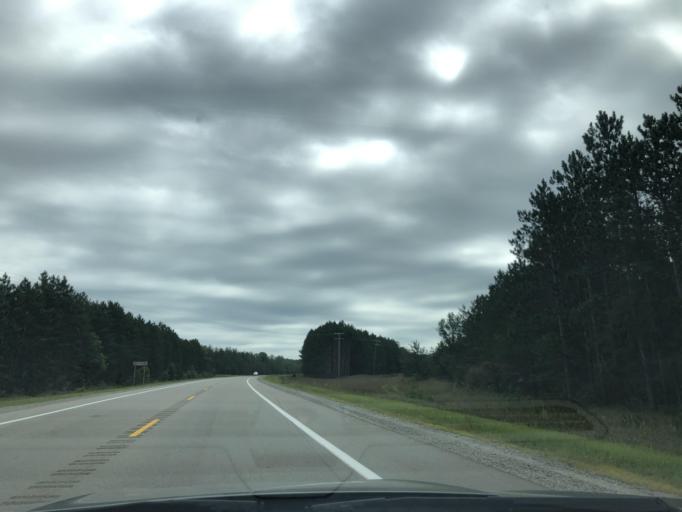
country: US
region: Michigan
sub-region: Clare County
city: Harrison
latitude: 44.0437
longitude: -85.0469
